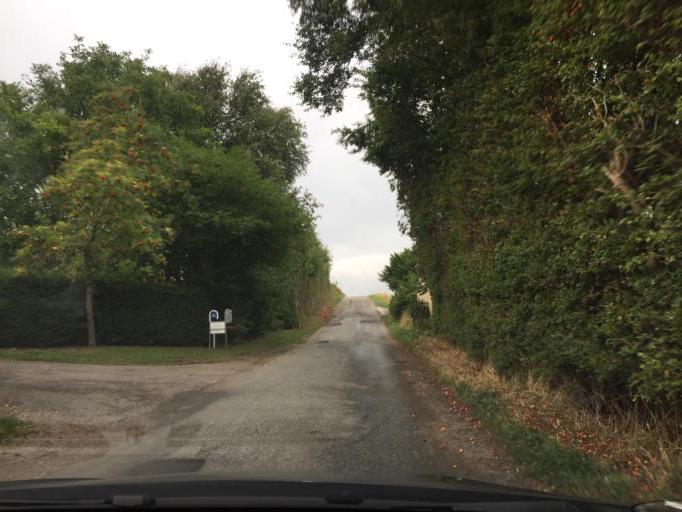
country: DK
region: South Denmark
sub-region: Assens Kommune
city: Harby
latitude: 55.2036
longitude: 10.0247
